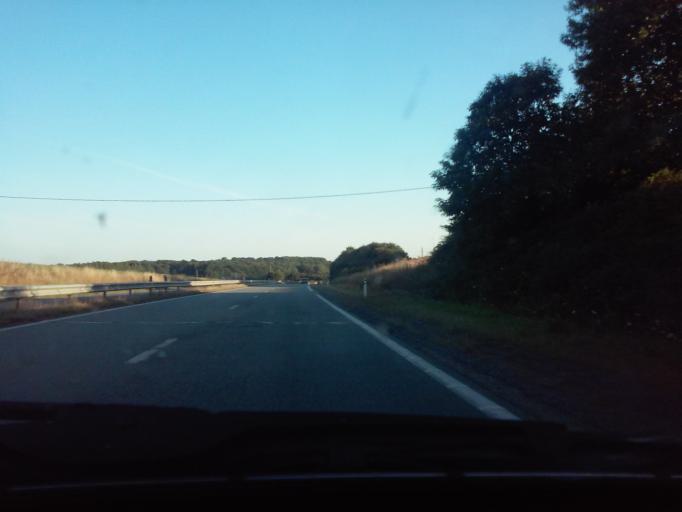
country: FR
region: Brittany
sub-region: Departement des Cotes-d'Armor
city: Saint-Samson-sur-Rance
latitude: 48.5051
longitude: -2.0394
